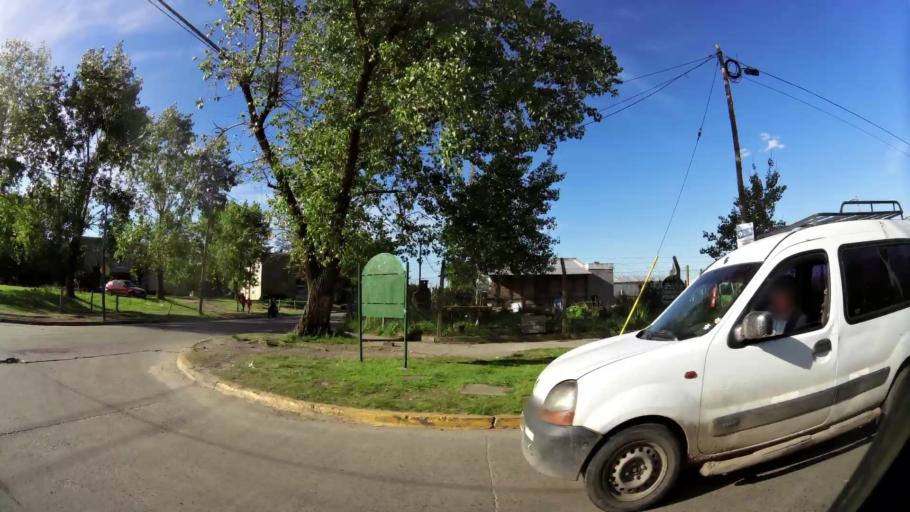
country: AR
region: Buenos Aires
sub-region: Partido de Almirante Brown
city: Adrogue
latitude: -34.8104
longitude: -58.3342
